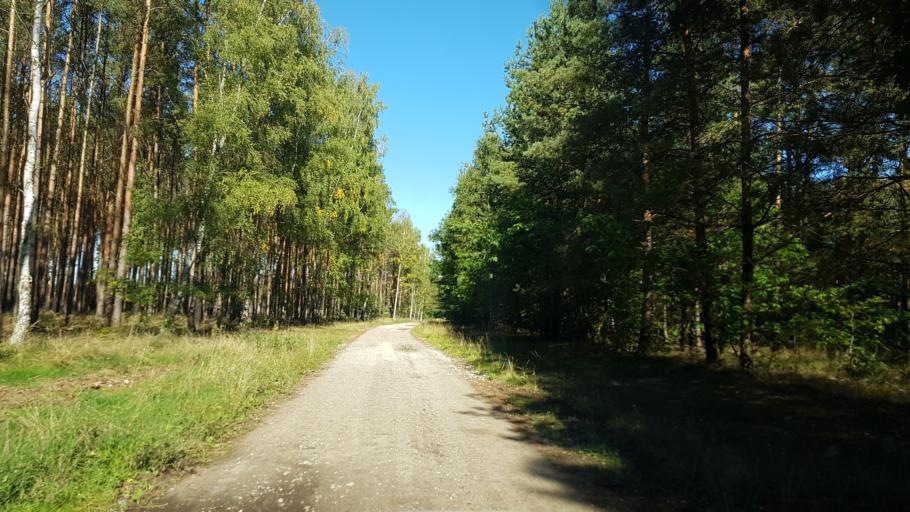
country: PL
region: Lubusz
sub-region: Powiat gorzowski
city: Lubiszyn
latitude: 52.8467
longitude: 14.9358
